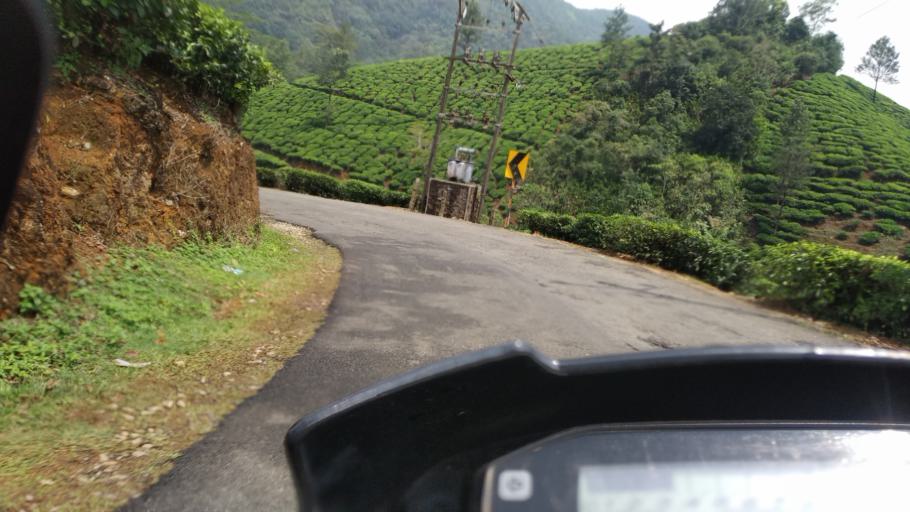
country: IN
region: Kerala
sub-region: Kottayam
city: Erattupetta
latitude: 9.6249
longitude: 76.9716
